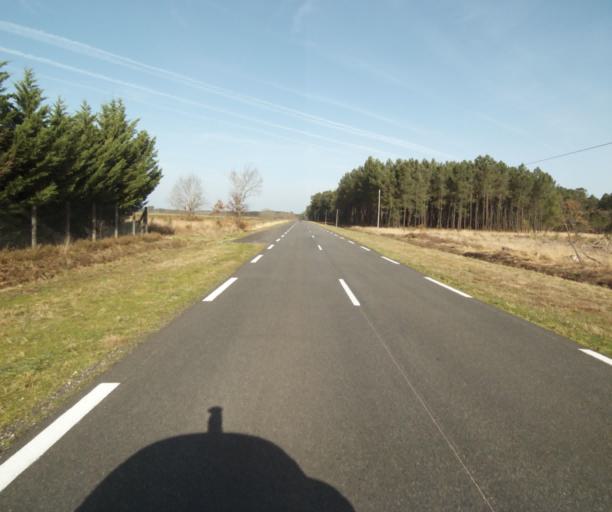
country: FR
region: Aquitaine
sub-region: Departement de la Gironde
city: Grignols
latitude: 44.1996
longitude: -0.1427
